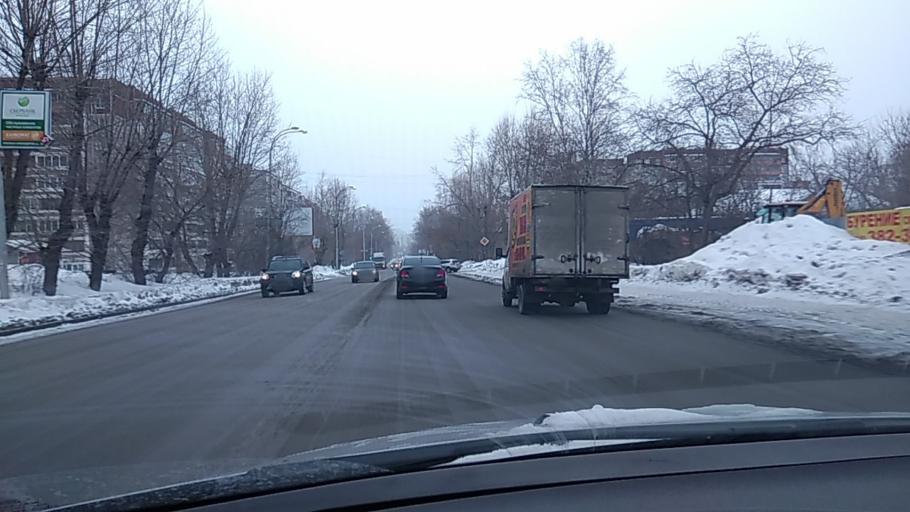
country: RU
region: Sverdlovsk
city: Yekaterinburg
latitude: 56.8979
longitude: 60.6300
